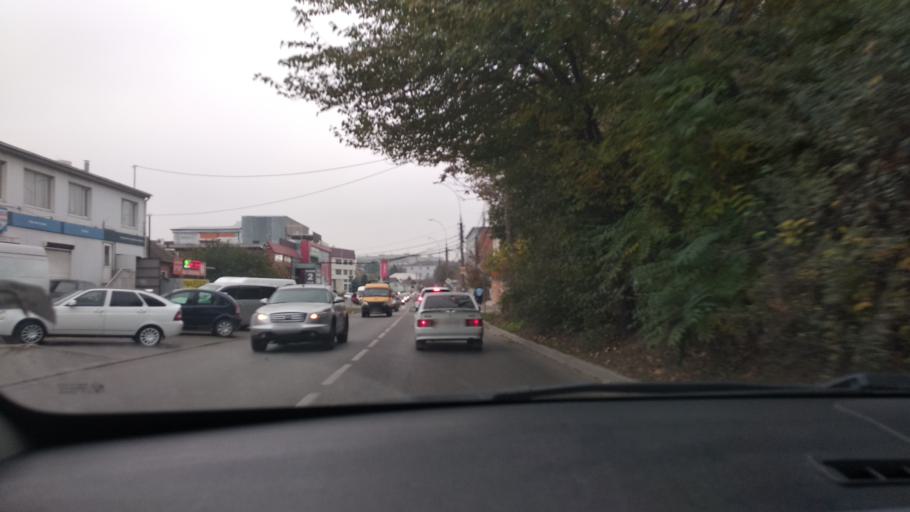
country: RU
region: Krasnodarskiy
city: Krasnodar
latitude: 45.0251
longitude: 39.0079
